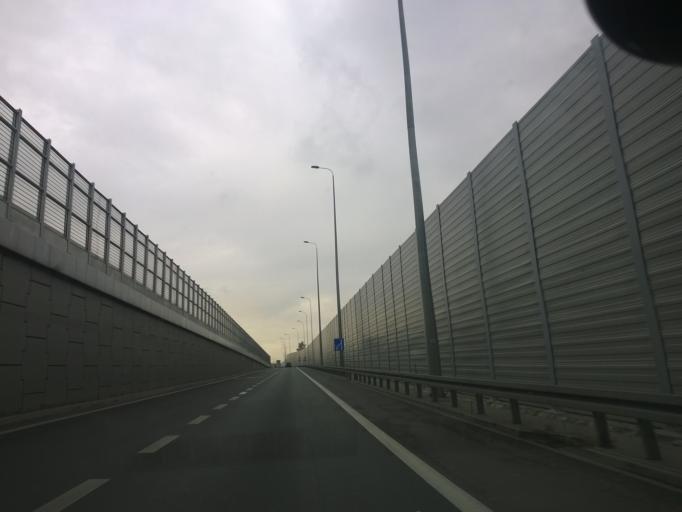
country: PL
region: Masovian Voivodeship
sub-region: Powiat pruszkowski
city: Raszyn
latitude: 52.1677
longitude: 20.9317
